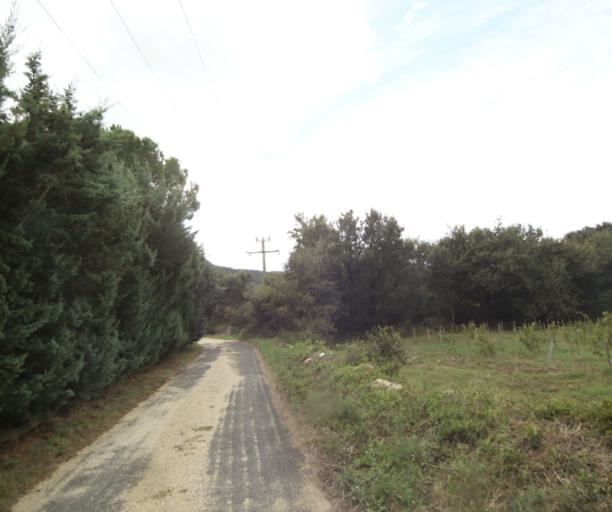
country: FR
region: Languedoc-Roussillon
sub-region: Departement des Pyrenees-Orientales
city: Argelers
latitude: 42.5358
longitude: 3.0000
